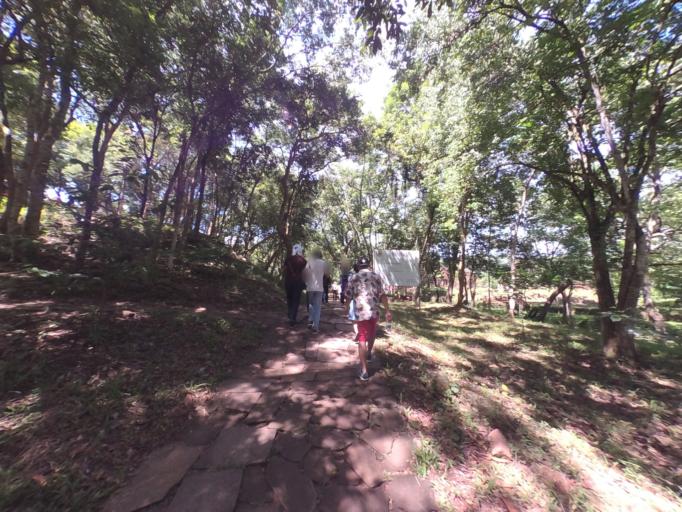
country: VN
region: Quang Nam
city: Dai Loc
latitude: 15.7636
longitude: 108.1249
